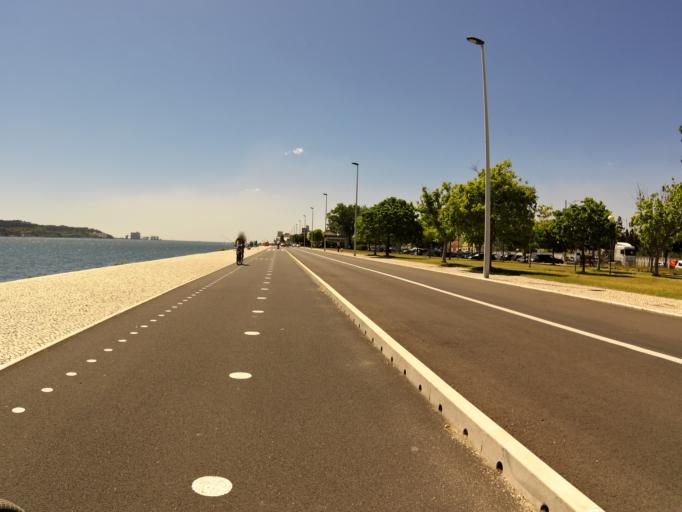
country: PT
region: Setubal
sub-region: Almada
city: Pragal
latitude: 38.6978
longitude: -9.1830
